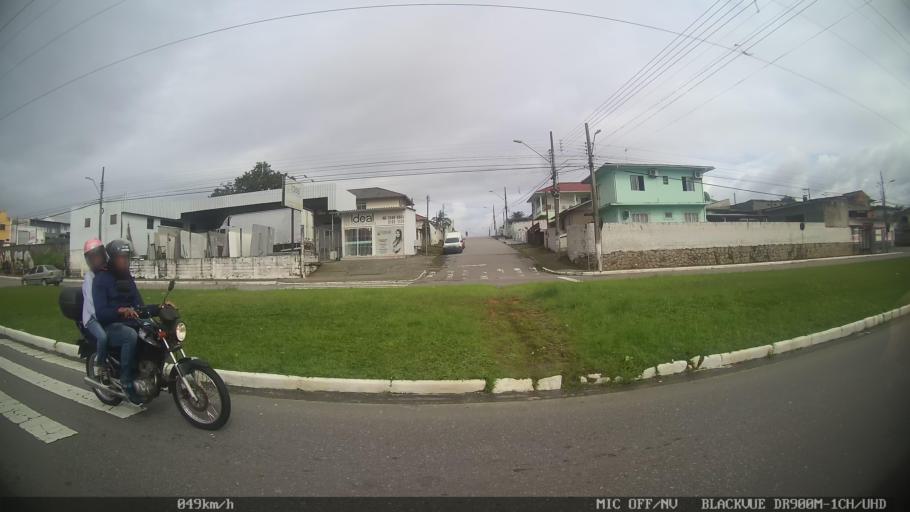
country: BR
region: Santa Catarina
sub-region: Sao Jose
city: Campinas
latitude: -27.5642
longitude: -48.6349
